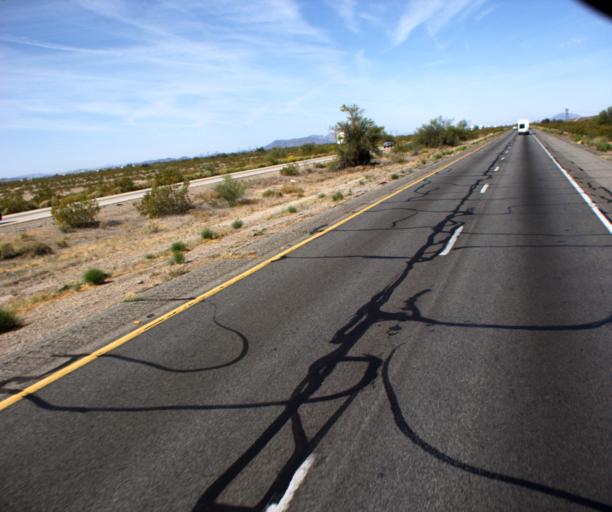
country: US
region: Arizona
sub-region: Maricopa County
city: Buckeye
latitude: 33.4473
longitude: -112.7125
